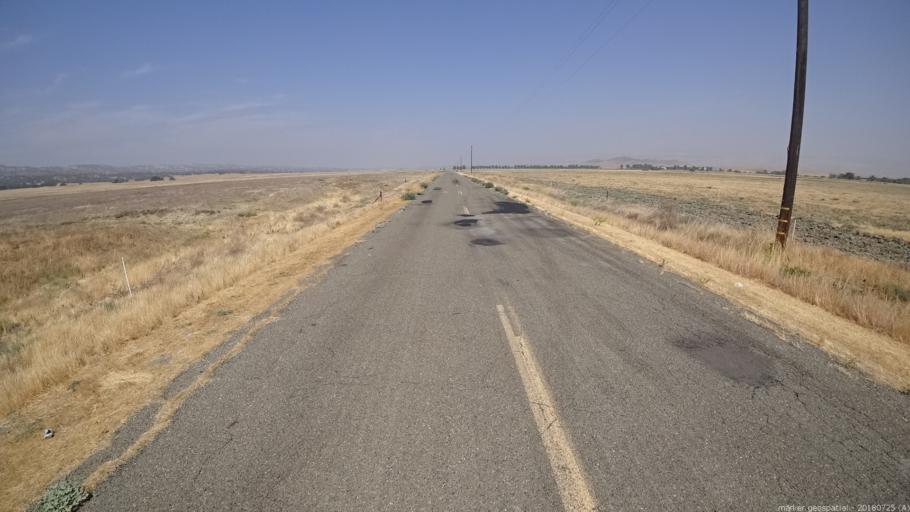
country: US
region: California
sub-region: San Luis Obispo County
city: Shandon
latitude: 35.7952
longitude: -120.3484
